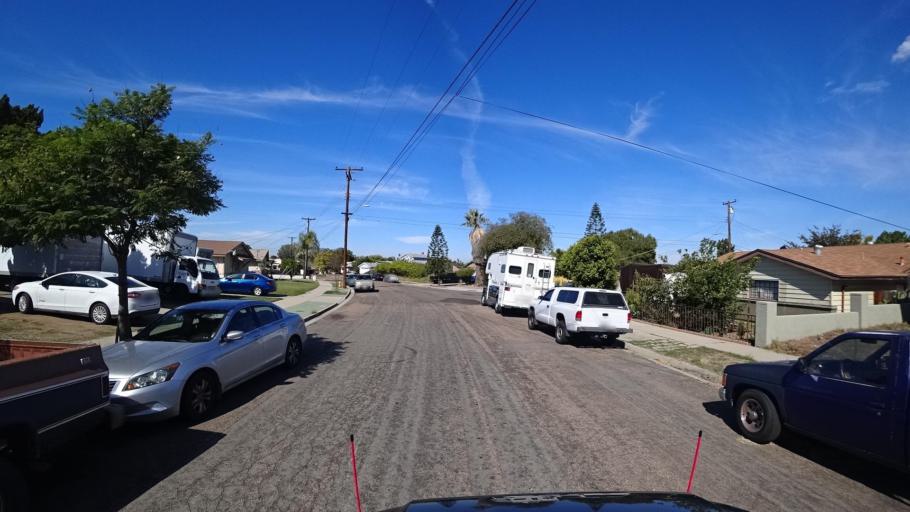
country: US
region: California
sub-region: San Diego County
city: La Presa
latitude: 32.7187
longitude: -117.0210
